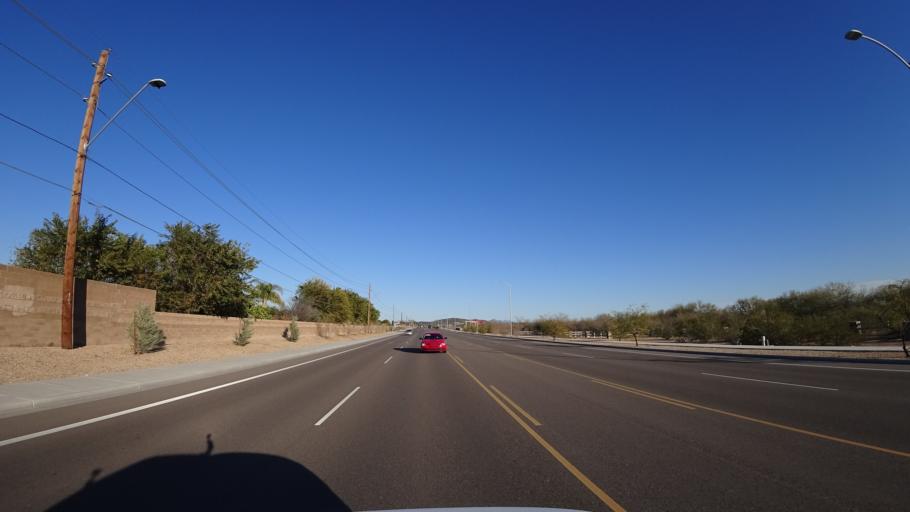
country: US
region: Arizona
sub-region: Maricopa County
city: Peoria
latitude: 33.6981
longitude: -112.1626
